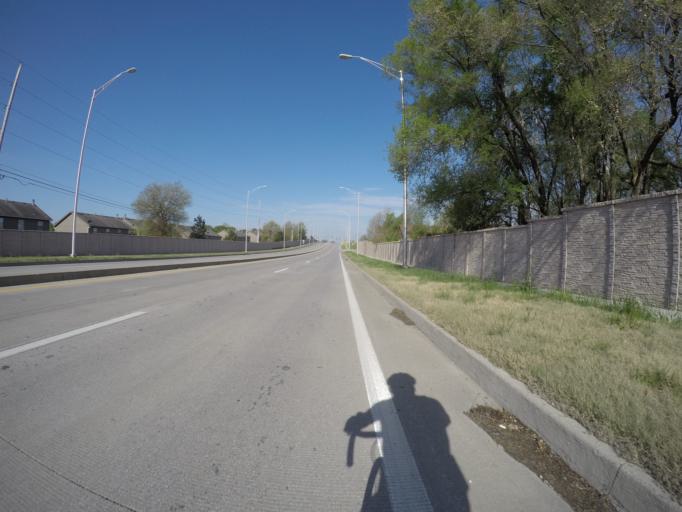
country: US
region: Missouri
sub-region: Cass County
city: Lake Winnebago
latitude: 38.8532
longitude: -94.3914
